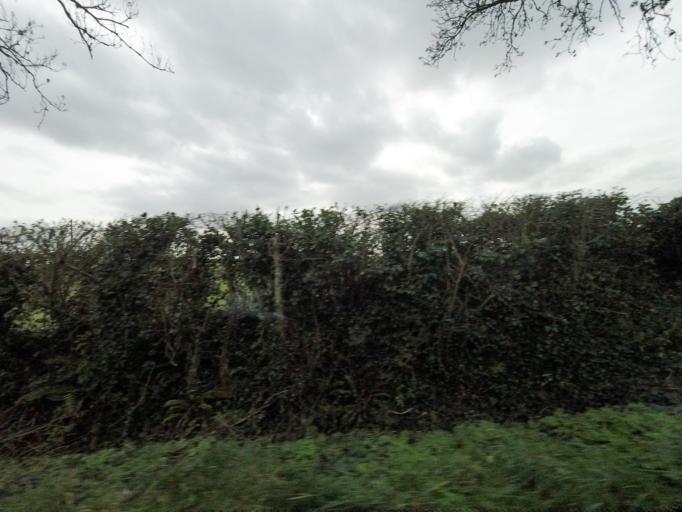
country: IE
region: Leinster
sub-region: Kildare
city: Eadestown
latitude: 53.1716
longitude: -6.6212
